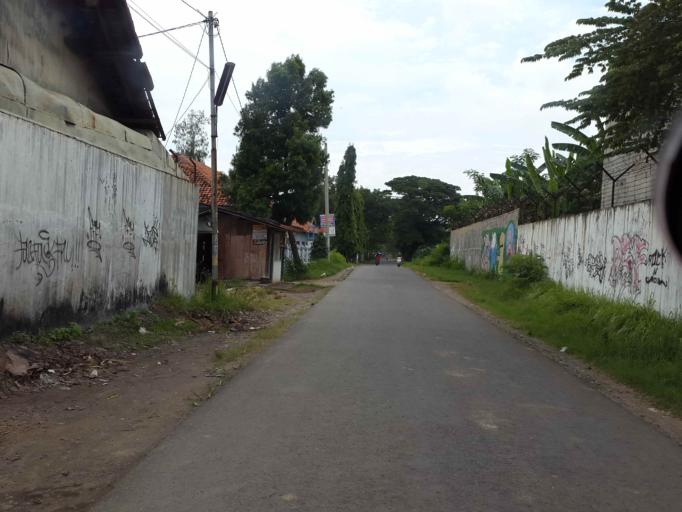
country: ID
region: Central Java
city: Comal
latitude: -6.8979
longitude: 109.5310
